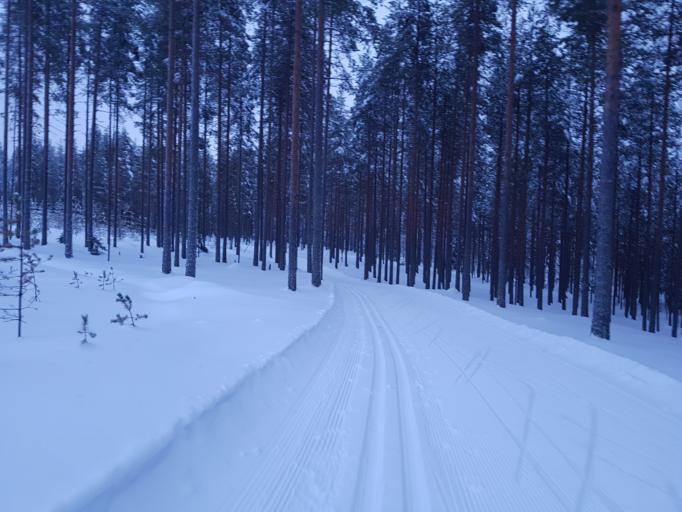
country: FI
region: Kainuu
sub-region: Kehys-Kainuu
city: Kuhmo
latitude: 64.0855
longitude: 29.5181
